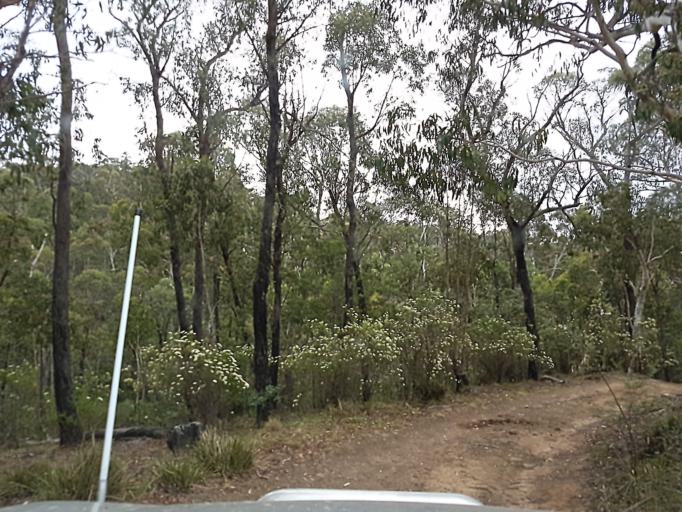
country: AU
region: New South Wales
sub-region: Snowy River
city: Jindabyne
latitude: -36.8650
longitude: 148.3260
